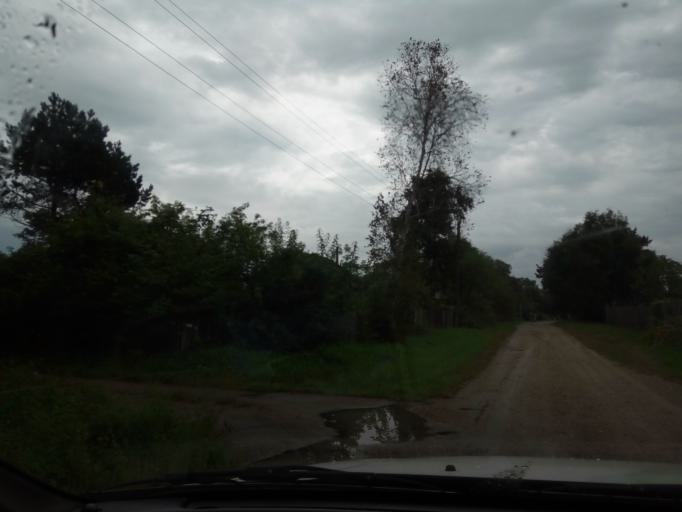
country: RU
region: Primorskiy
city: Lazo
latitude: 45.8708
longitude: 133.6538
